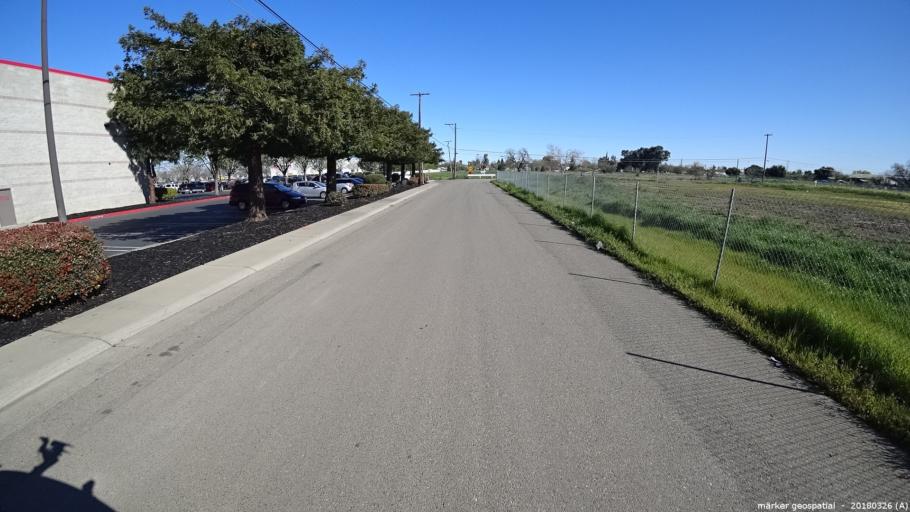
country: US
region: California
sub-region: Sacramento County
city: Florin
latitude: 38.4683
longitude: -121.4131
